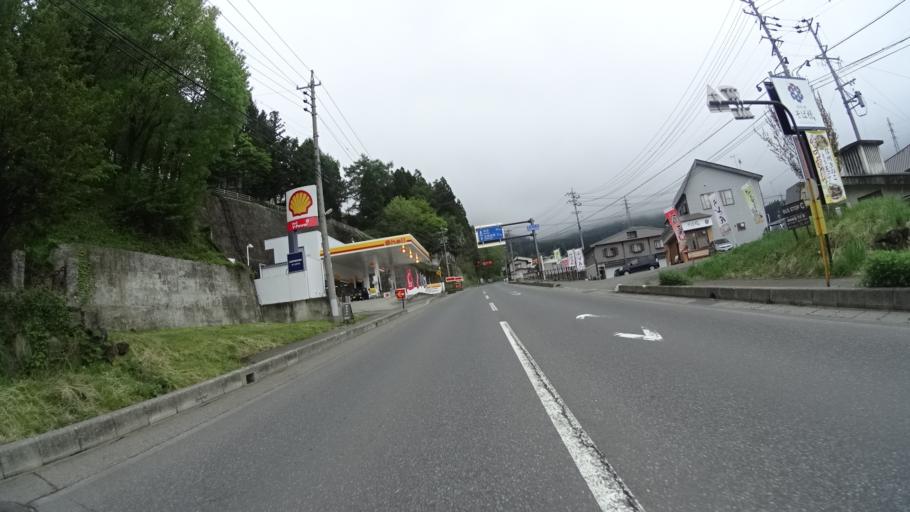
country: JP
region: Nagano
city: Nakano
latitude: 36.7292
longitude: 138.4404
